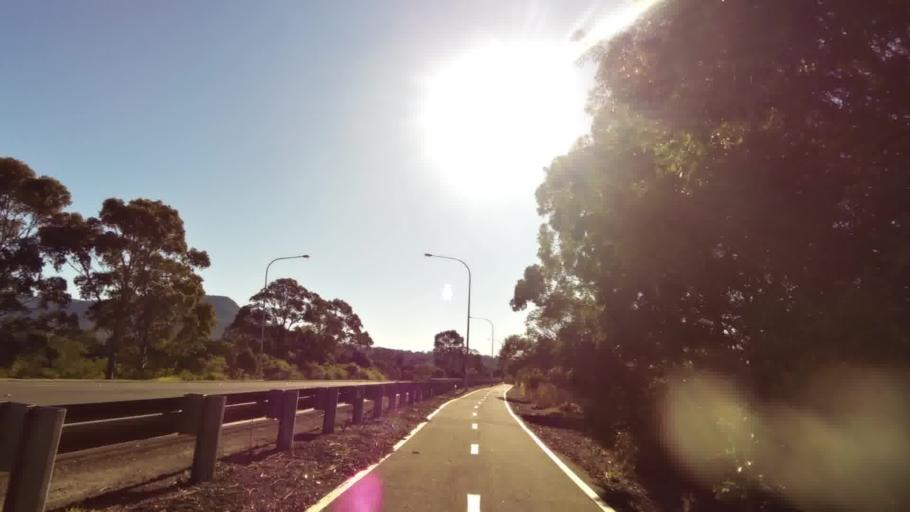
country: AU
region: New South Wales
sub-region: Wollongong
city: Koonawarra
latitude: -34.4821
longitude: 150.8032
